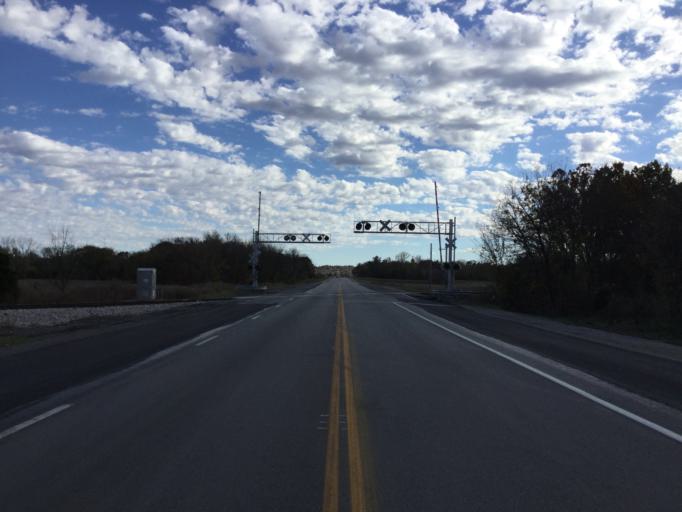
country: US
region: Kansas
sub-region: Montgomery County
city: Cherryvale
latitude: 37.1847
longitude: -95.5787
